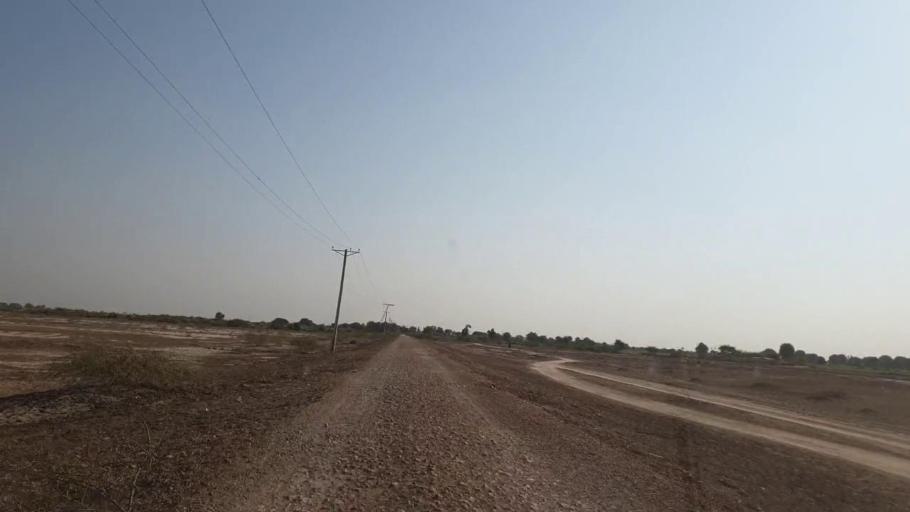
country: PK
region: Sindh
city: Naukot
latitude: 25.0152
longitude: 69.4746
